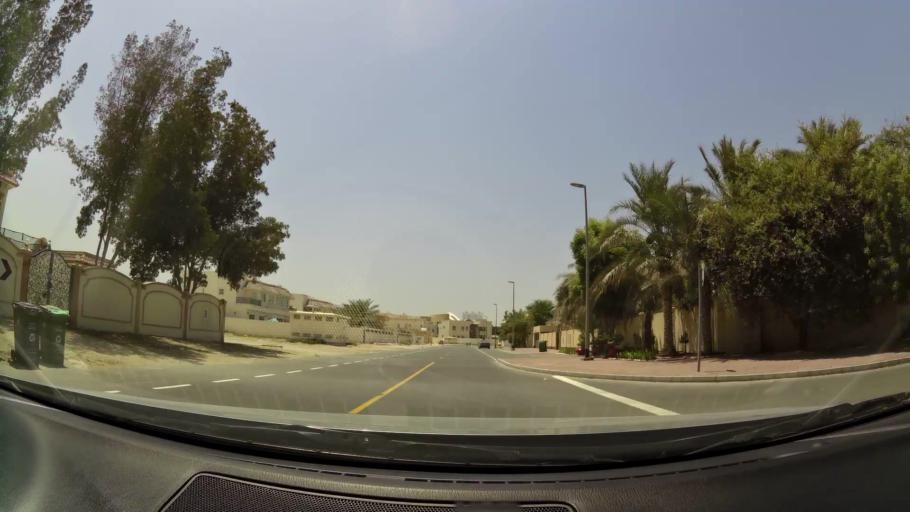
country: AE
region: Dubai
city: Dubai
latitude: 25.0976
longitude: 55.2081
